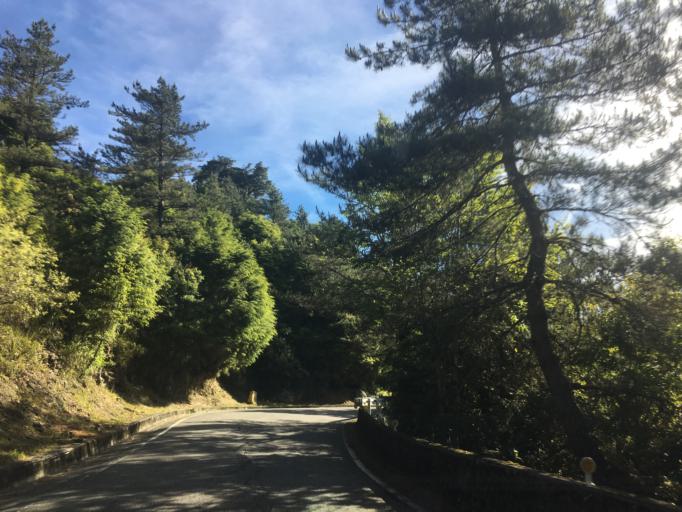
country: TW
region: Taiwan
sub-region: Nantou
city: Puli
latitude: 24.1129
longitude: 121.2274
